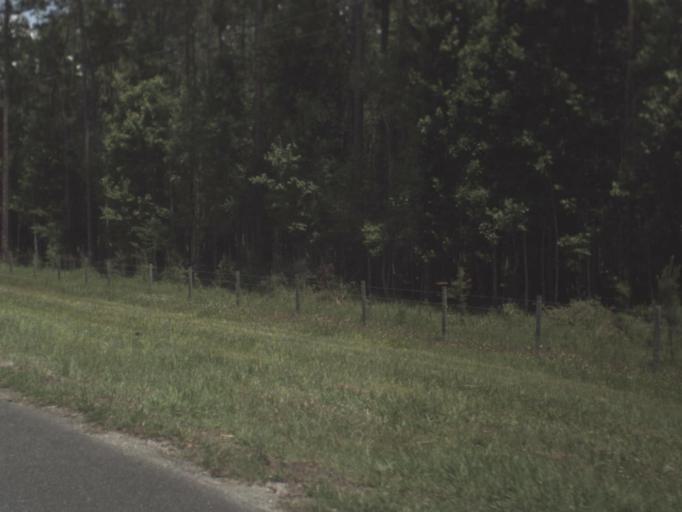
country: US
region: Florida
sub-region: Union County
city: Lake Butler
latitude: 30.0392
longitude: -82.3813
